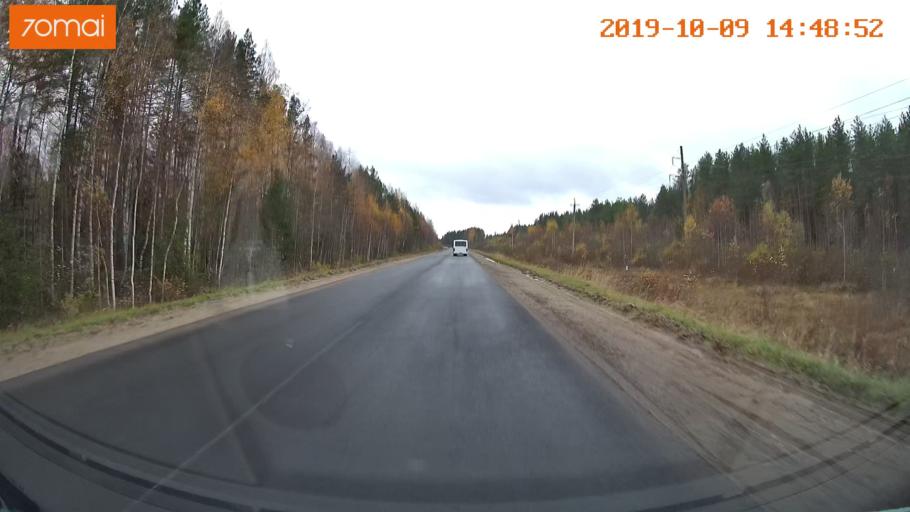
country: RU
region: Kostroma
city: Chistyye Bory
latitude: 58.4003
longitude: 41.5776
